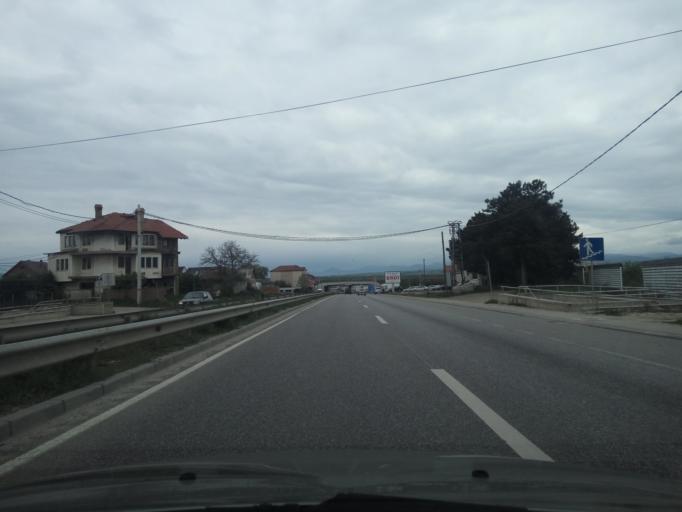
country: XK
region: Pristina
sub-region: Kosovo Polje
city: Kosovo Polje
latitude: 42.6981
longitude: 21.1131
